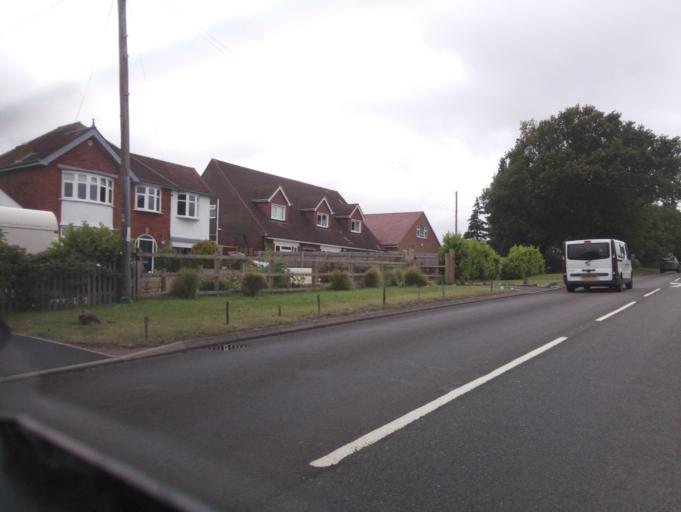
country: GB
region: England
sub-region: Staffordshire
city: Burton upon Trent
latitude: 52.8422
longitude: -1.6714
